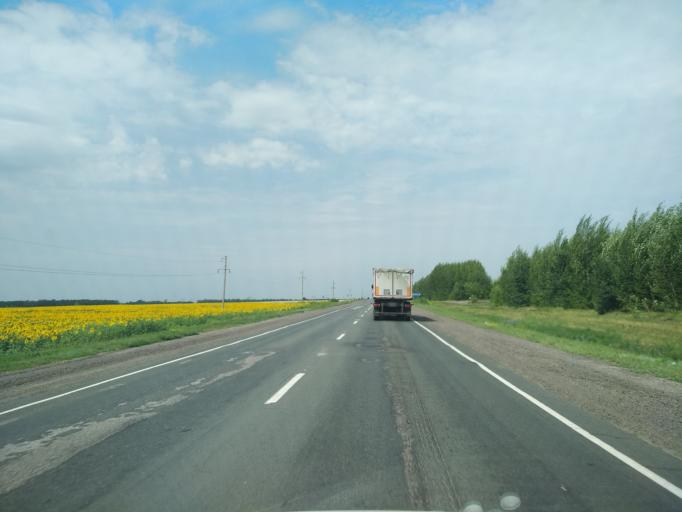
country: RU
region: Voronezj
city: Orlovo
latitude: 51.6768
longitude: 39.6965
